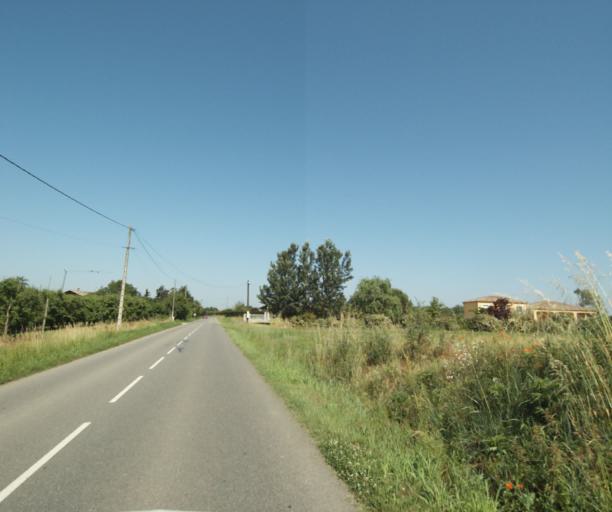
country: FR
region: Midi-Pyrenees
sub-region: Departement du Tarn-et-Garonne
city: Montbeton
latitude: 44.0282
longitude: 1.3138
